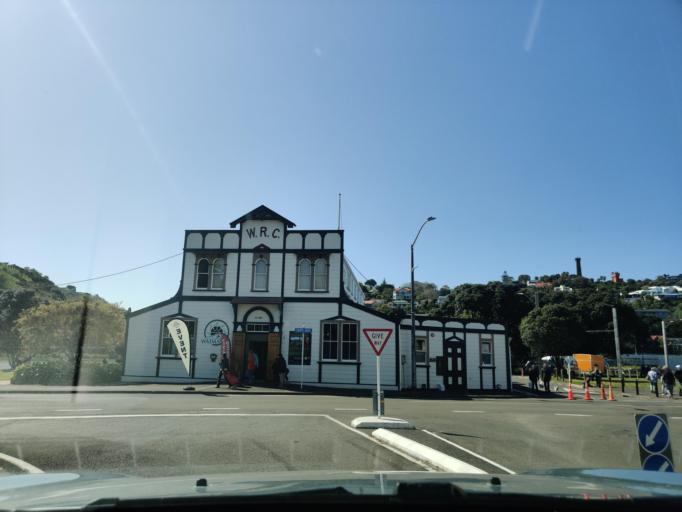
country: NZ
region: Manawatu-Wanganui
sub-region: Wanganui District
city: Wanganui
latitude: -39.9326
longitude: 175.0572
